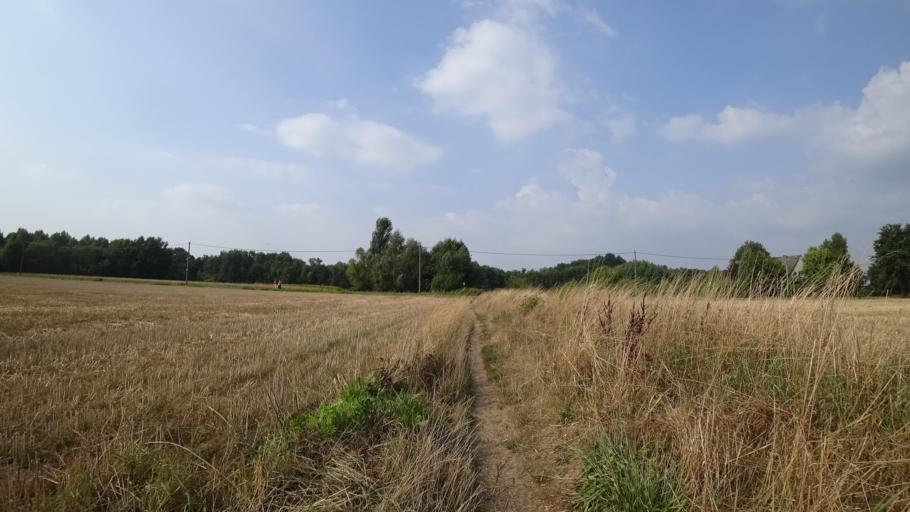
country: DE
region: North Rhine-Westphalia
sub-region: Regierungsbezirk Detmold
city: Guetersloh
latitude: 51.9339
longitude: 8.4334
